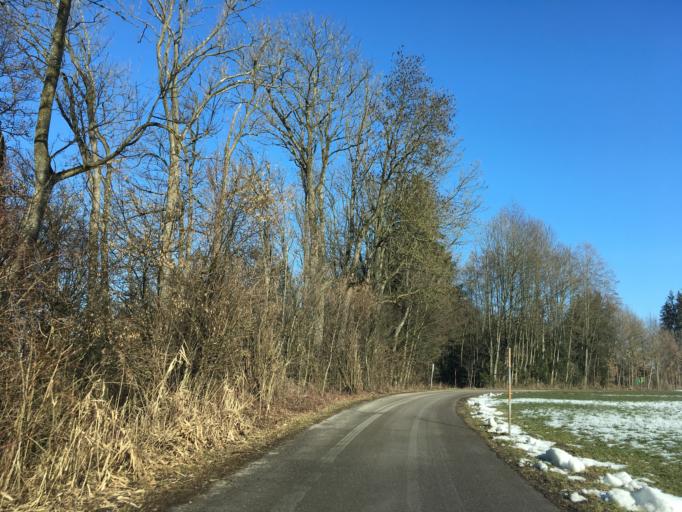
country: DE
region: Bavaria
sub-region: Upper Bavaria
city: Vogtareuth
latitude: 47.9417
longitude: 12.1682
